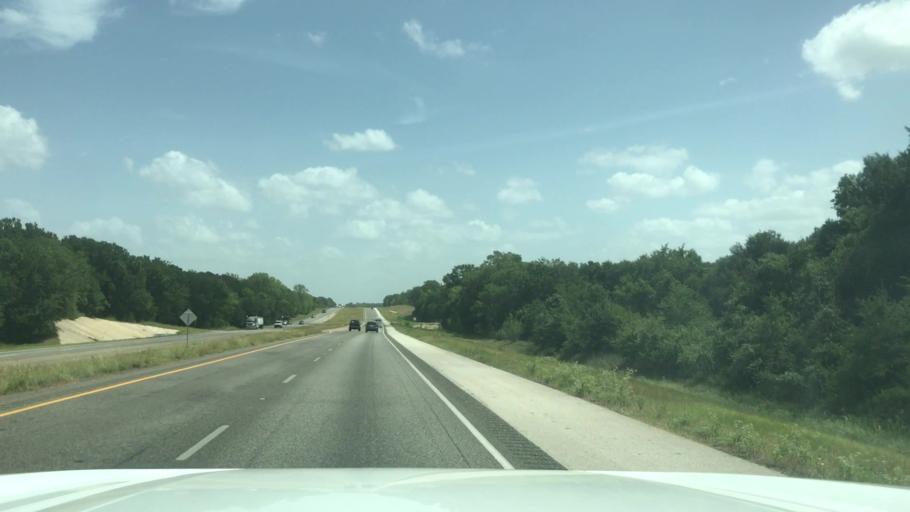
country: US
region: Texas
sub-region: Robertson County
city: Calvert
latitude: 30.9453
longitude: -96.6464
